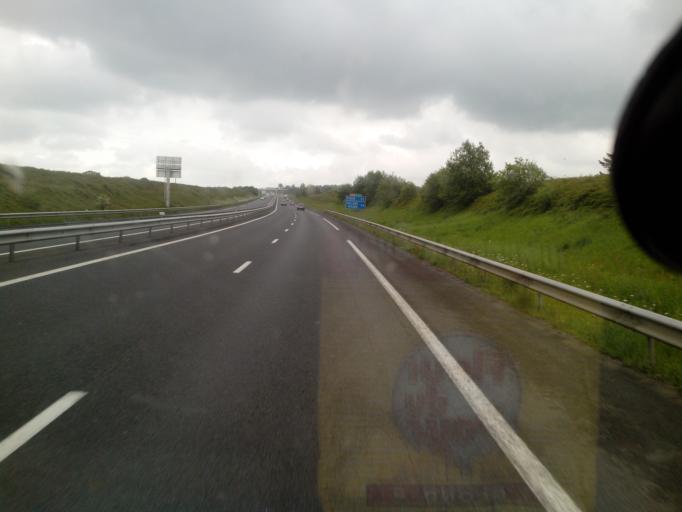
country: FR
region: Lower Normandy
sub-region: Departement de la Manche
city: Saint-Amand
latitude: 48.9854
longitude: -0.9356
